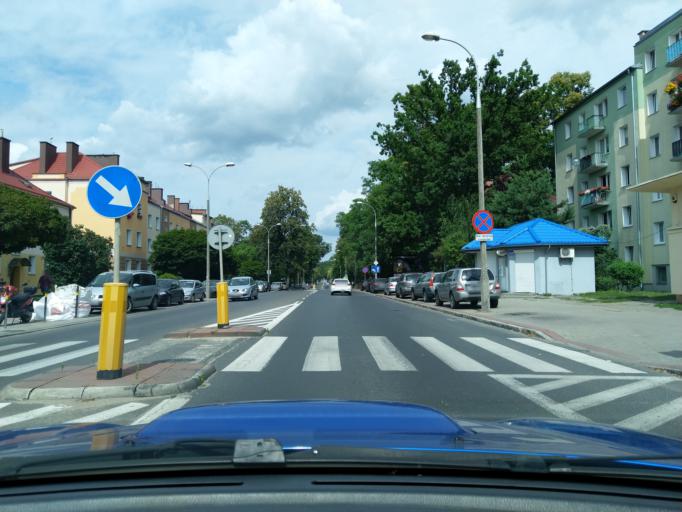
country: PL
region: Warmian-Masurian Voivodeship
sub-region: Powiat olsztynski
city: Olsztyn
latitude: 53.7909
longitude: 20.4824
